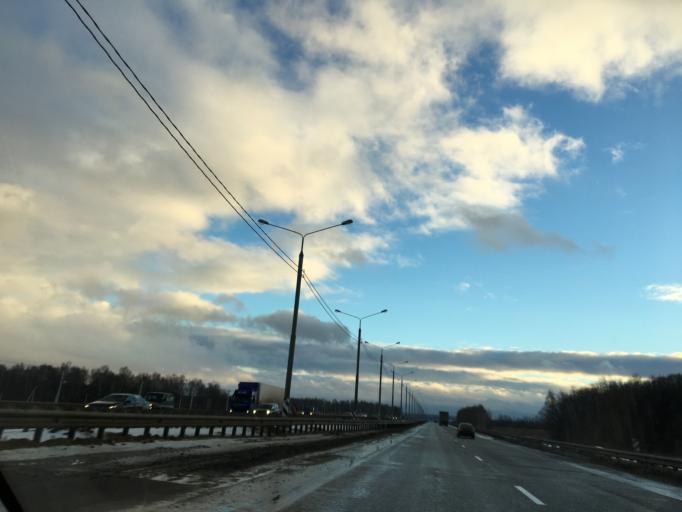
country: RU
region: Tula
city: Zaokskiy
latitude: 54.8014
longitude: 37.4847
